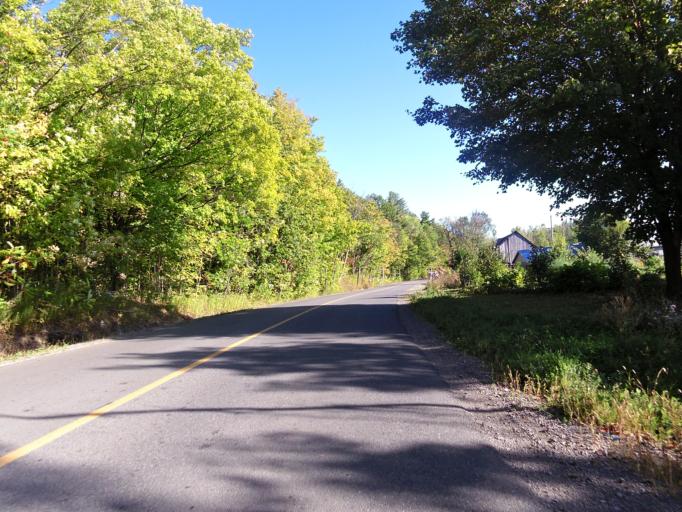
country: CA
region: Quebec
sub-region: Outaouais
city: Wakefield
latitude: 45.4991
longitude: -75.9167
